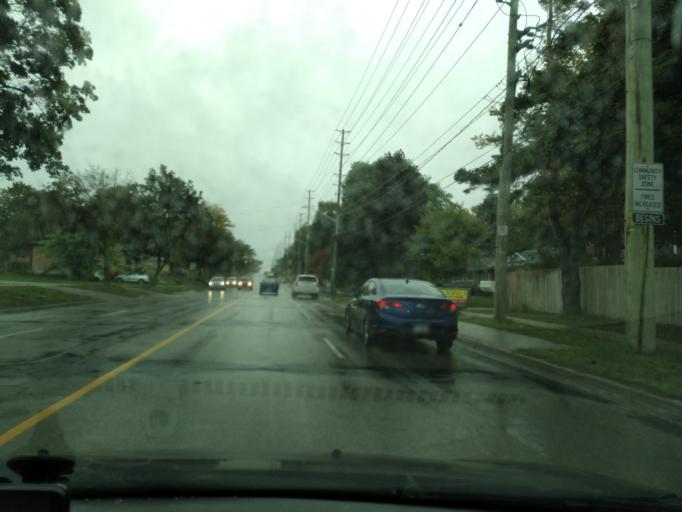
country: CA
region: Ontario
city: Barrie
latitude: 44.3906
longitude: -79.7121
